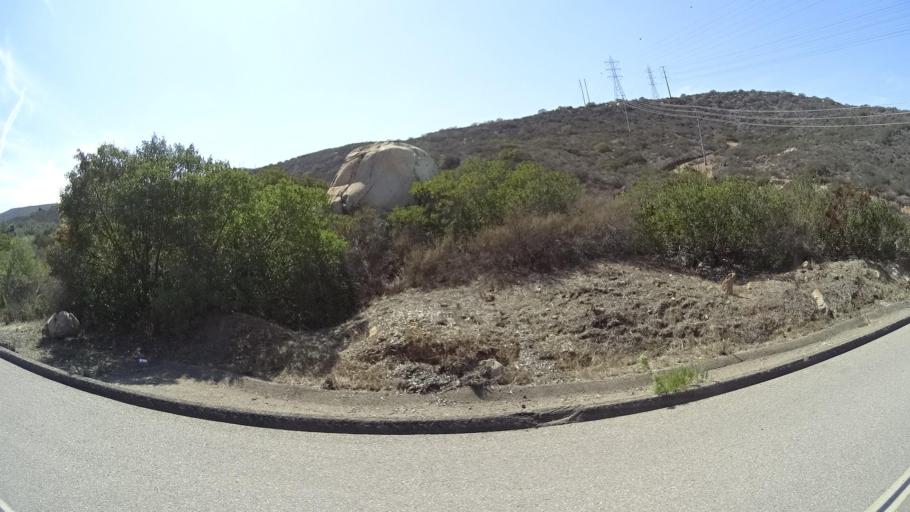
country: US
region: California
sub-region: San Diego County
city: Rancho San Diego
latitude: 32.7214
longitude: -116.9301
